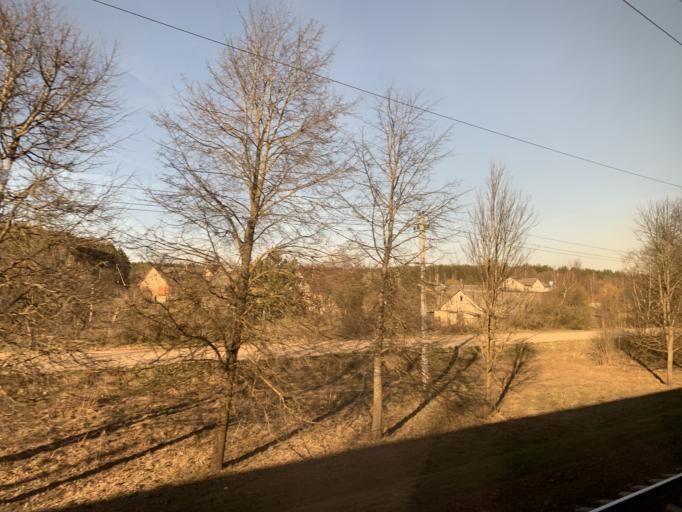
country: BY
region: Minsk
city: Pyatryshki
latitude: 54.1032
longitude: 27.1533
